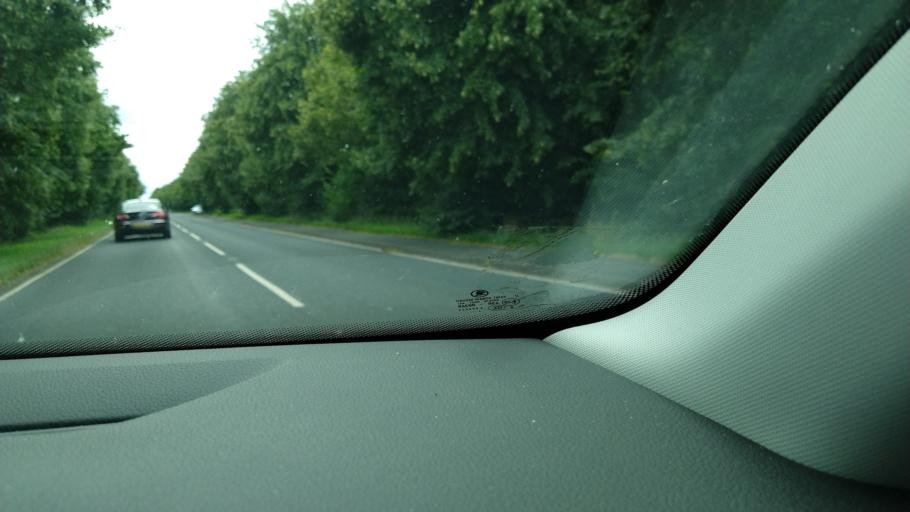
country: GB
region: England
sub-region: North Yorkshire
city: Camblesforth
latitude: 53.7274
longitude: -1.0059
